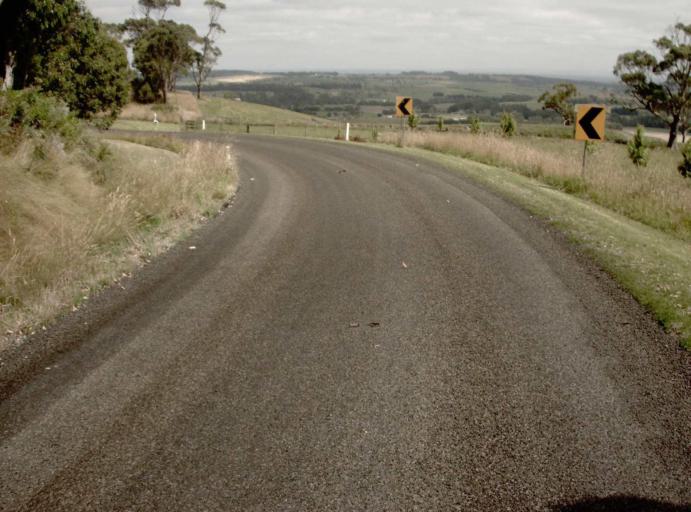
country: AU
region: Victoria
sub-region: Cardinia
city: Bunyip
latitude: -38.3314
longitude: 145.7240
